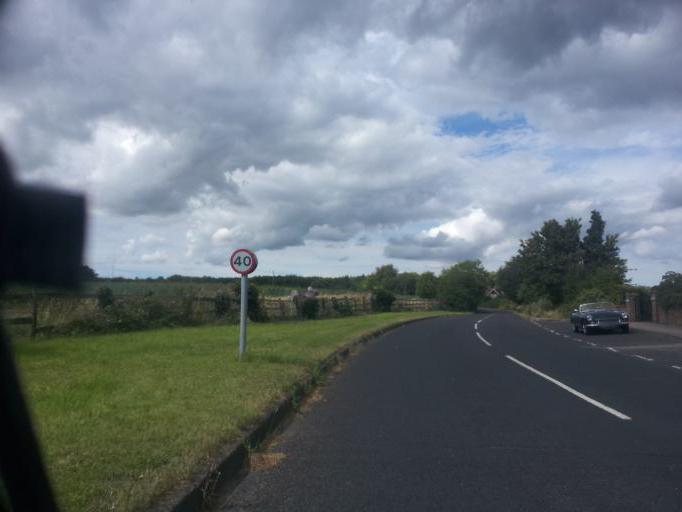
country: GB
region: England
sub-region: Kent
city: Wateringbury
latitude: 51.2621
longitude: 0.4311
